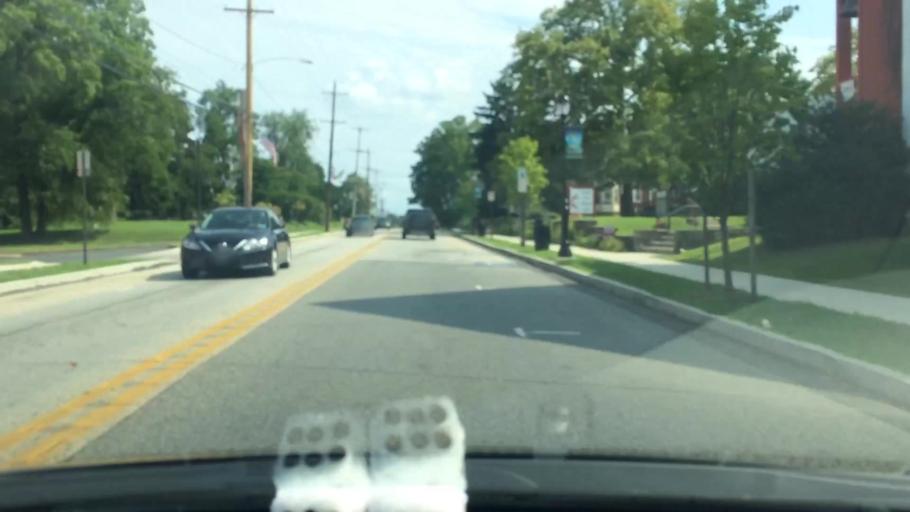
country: US
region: Pennsylvania
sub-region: Delaware County
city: Prospect Park
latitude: 39.8851
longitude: -75.3080
